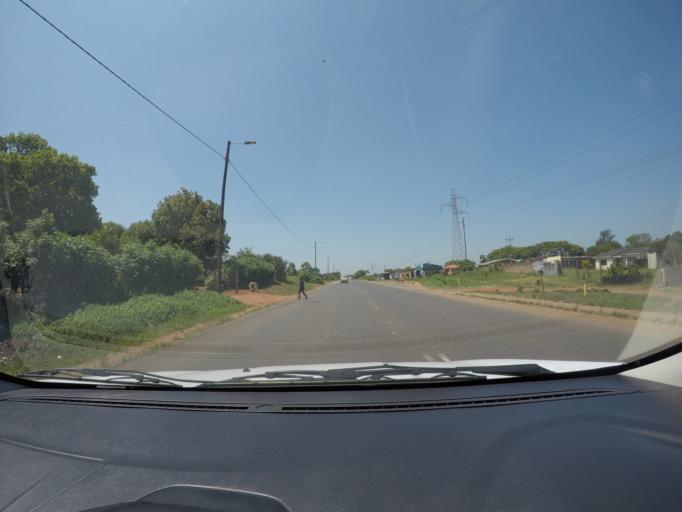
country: ZA
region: KwaZulu-Natal
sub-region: uThungulu District Municipality
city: eSikhawini
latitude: -28.8381
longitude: 31.9369
